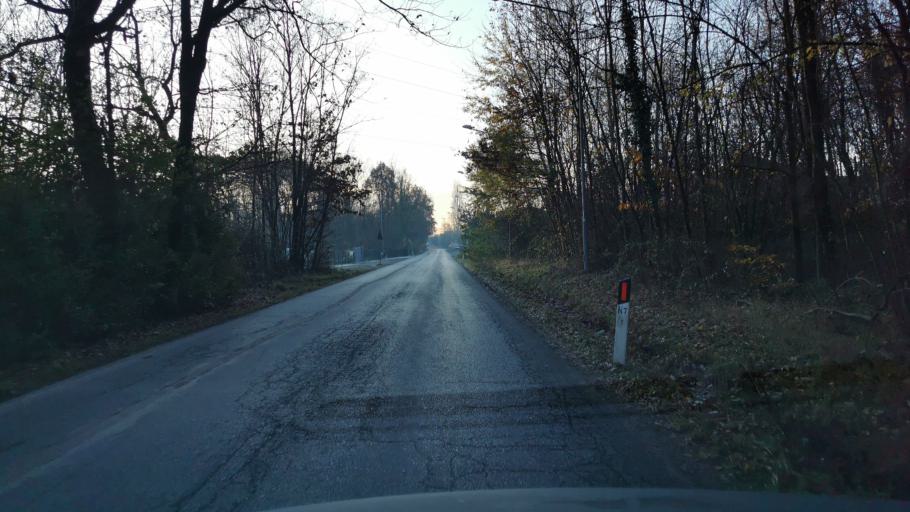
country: IT
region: Piedmont
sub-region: Provincia di Torino
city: La Cassa
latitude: 45.1751
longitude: 7.5186
